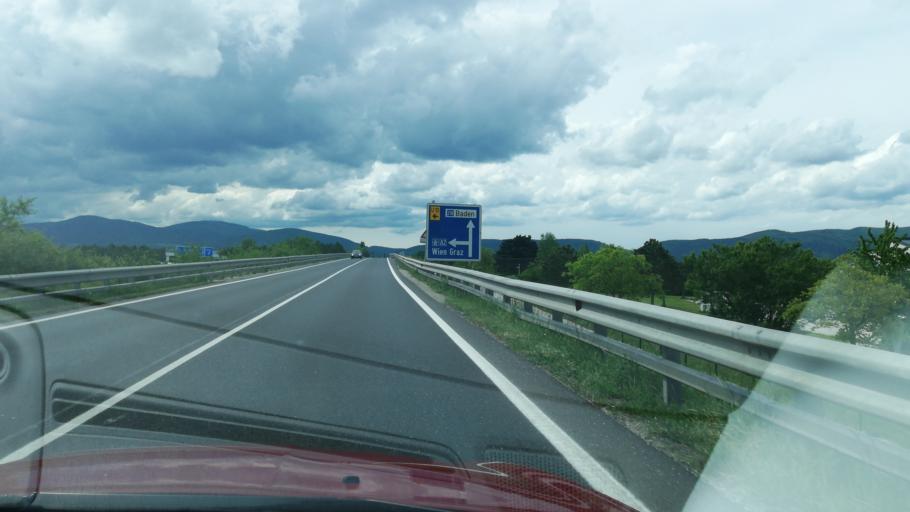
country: AT
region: Lower Austria
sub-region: Politischer Bezirk Baden
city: Traiskirchen
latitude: 47.9884
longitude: 16.2845
